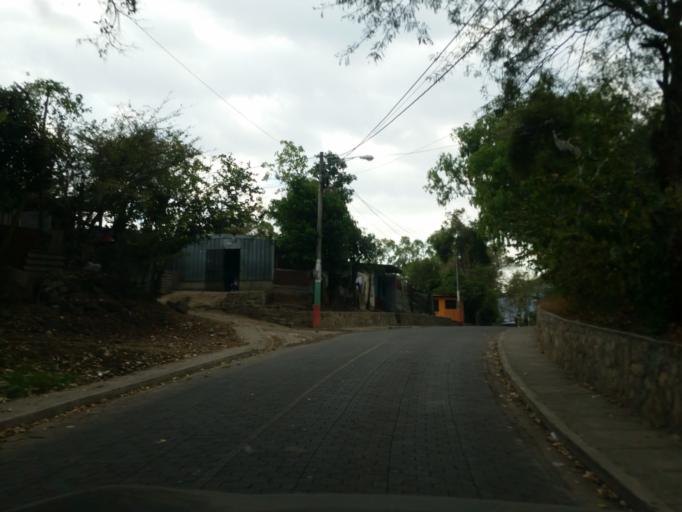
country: NI
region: Jinotega
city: Jinotega
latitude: 13.1049
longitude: -86.0038
